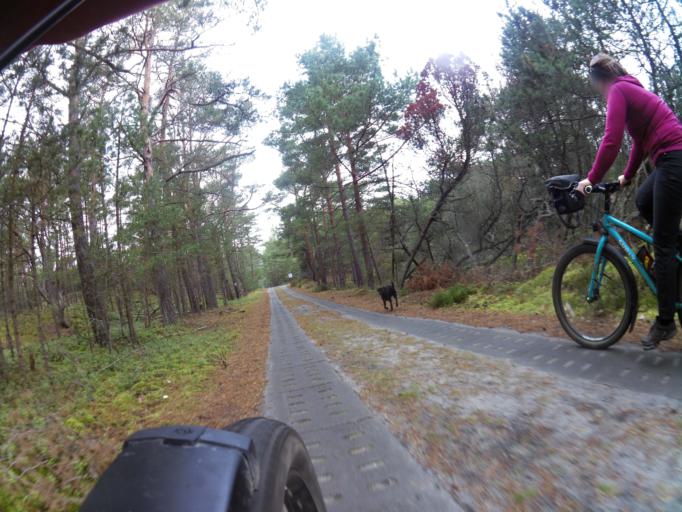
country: PL
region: Pomeranian Voivodeship
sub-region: Powiat pucki
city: Hel
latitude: 54.6224
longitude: 18.8191
